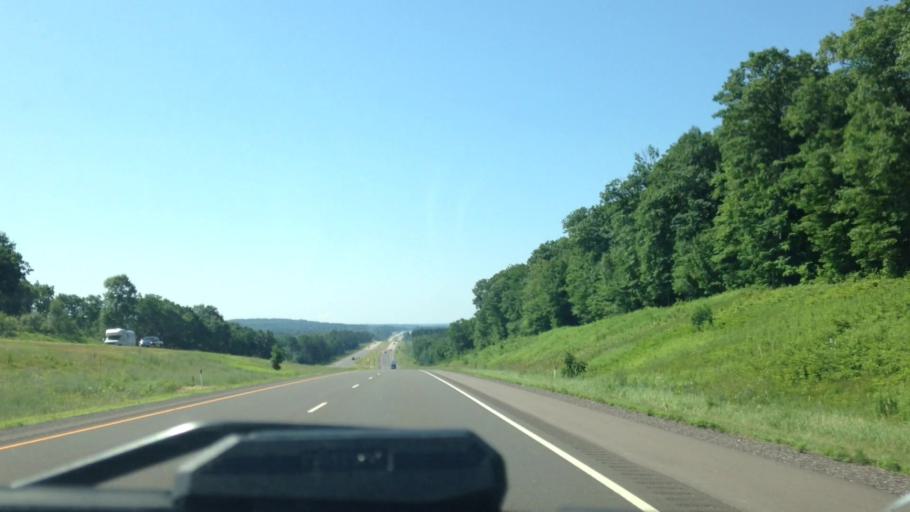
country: US
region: Wisconsin
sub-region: Washburn County
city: Spooner
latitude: 45.9334
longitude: -91.8280
